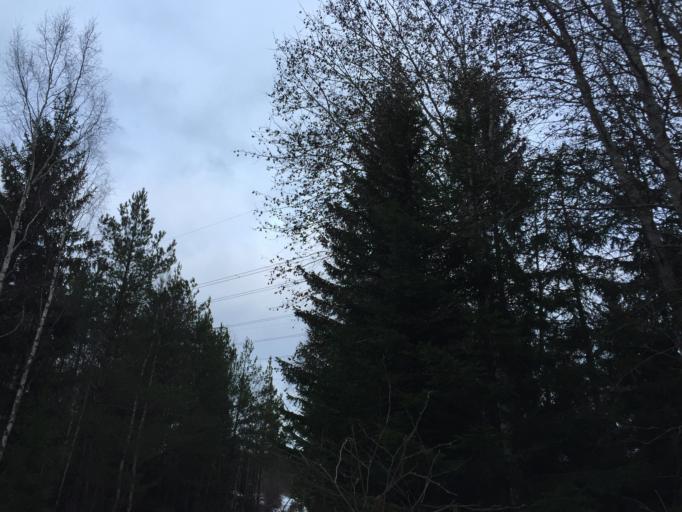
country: SE
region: Stockholm
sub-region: Salems Kommun
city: Ronninge
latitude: 59.2278
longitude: 17.6922
